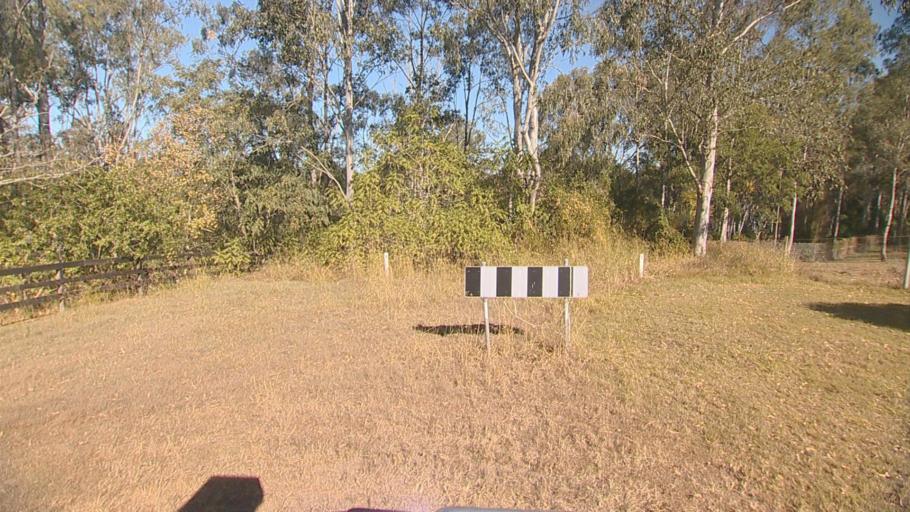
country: AU
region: Queensland
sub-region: Logan
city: North Maclean
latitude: -27.7785
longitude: 153.0245
